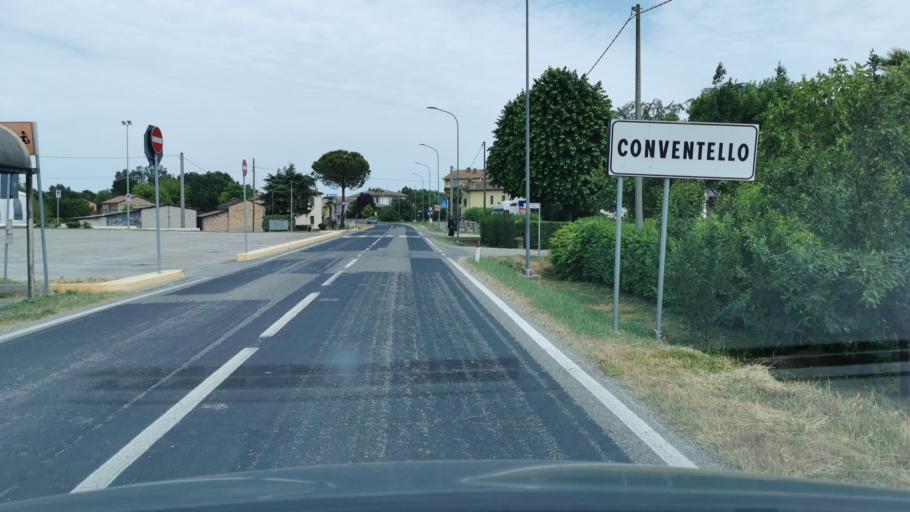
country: IT
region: Emilia-Romagna
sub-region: Provincia di Ravenna
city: Savarna-Conventella
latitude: 44.5007
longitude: 12.0954
